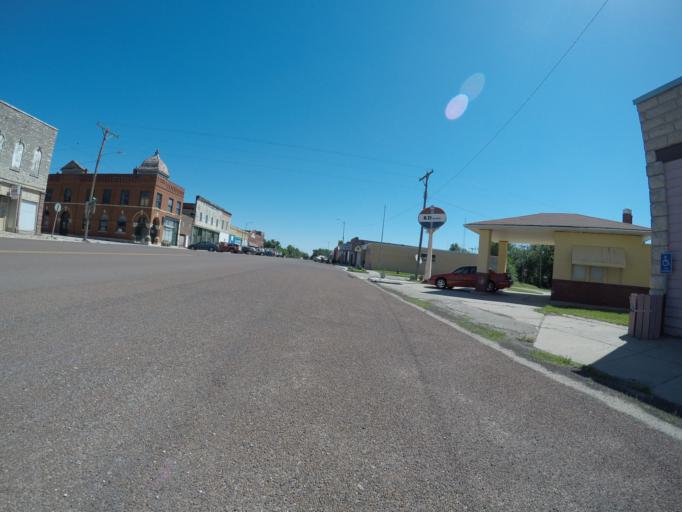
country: US
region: Kansas
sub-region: Wabaunsee County
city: Alma
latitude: 38.8593
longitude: -96.1084
